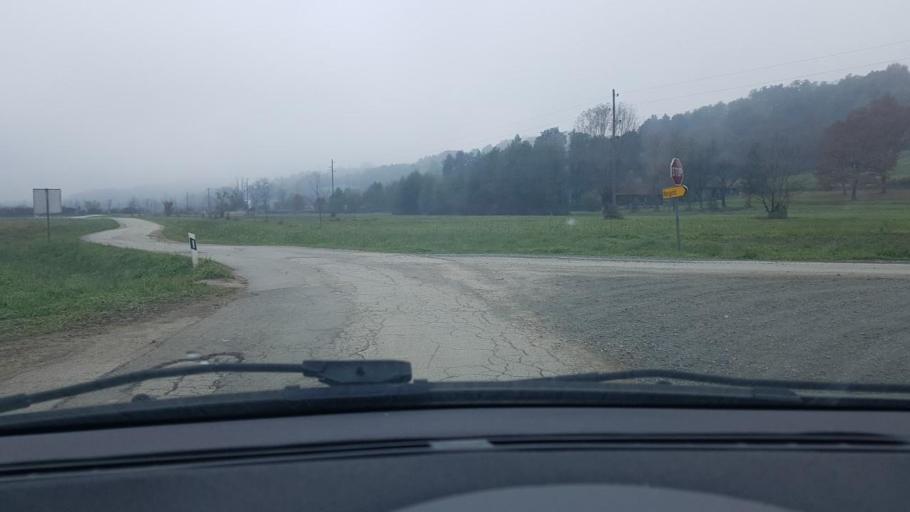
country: HR
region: Krapinsko-Zagorska
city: Zlatar
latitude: 46.1008
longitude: 16.1744
